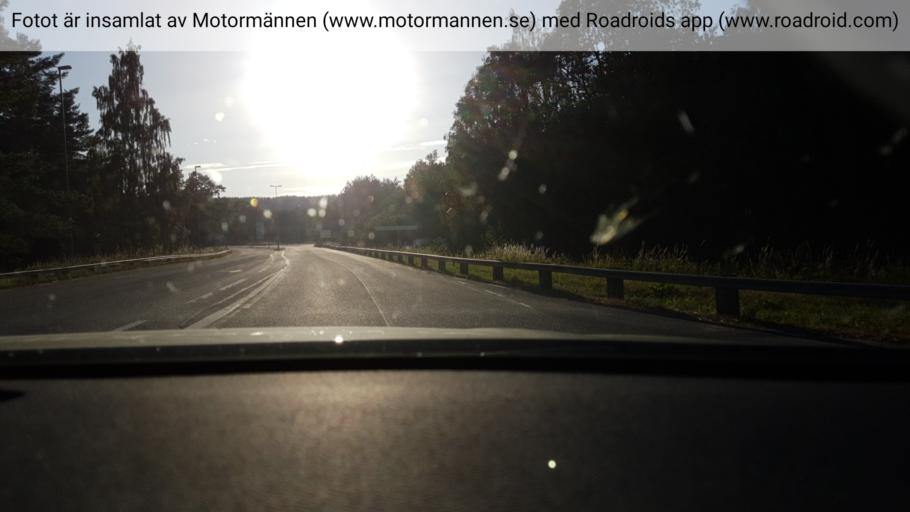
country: SE
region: Vaestra Goetaland
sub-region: Skovde Kommun
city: Skoevde
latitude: 58.4232
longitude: 13.8608
